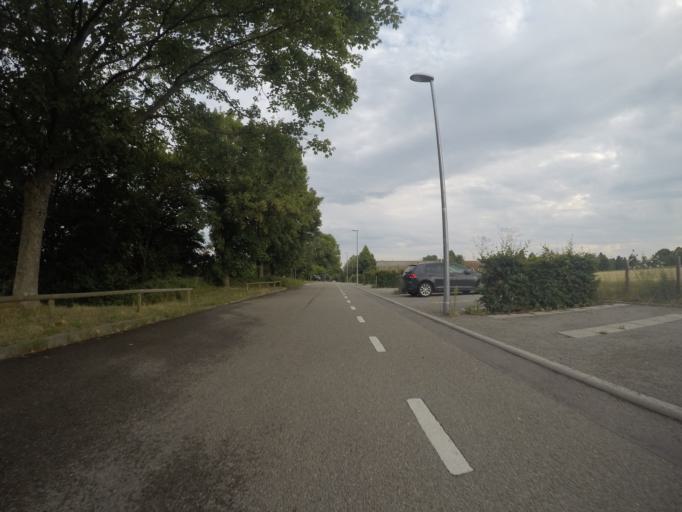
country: DE
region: Baden-Wuerttemberg
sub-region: Regierungsbezirk Stuttgart
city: Ostfildern
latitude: 48.7150
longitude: 9.2159
